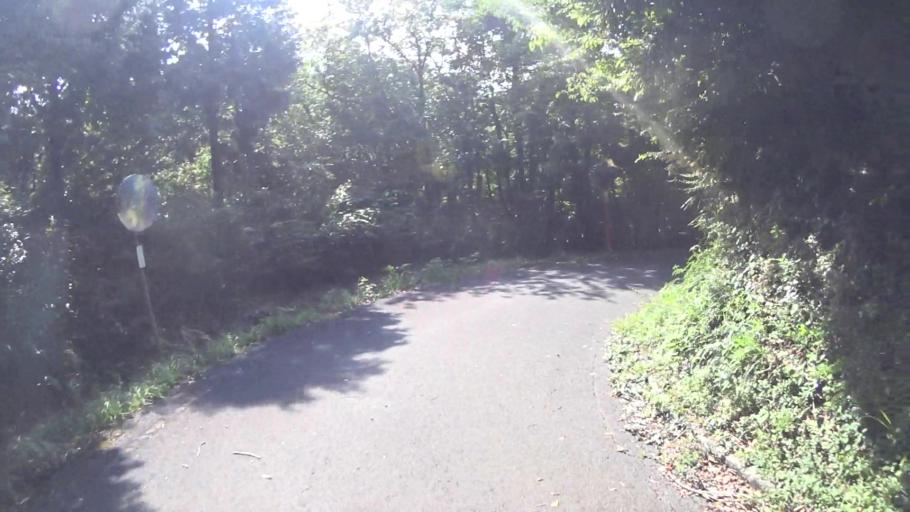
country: JP
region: Kyoto
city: Miyazu
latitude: 35.6572
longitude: 135.2415
